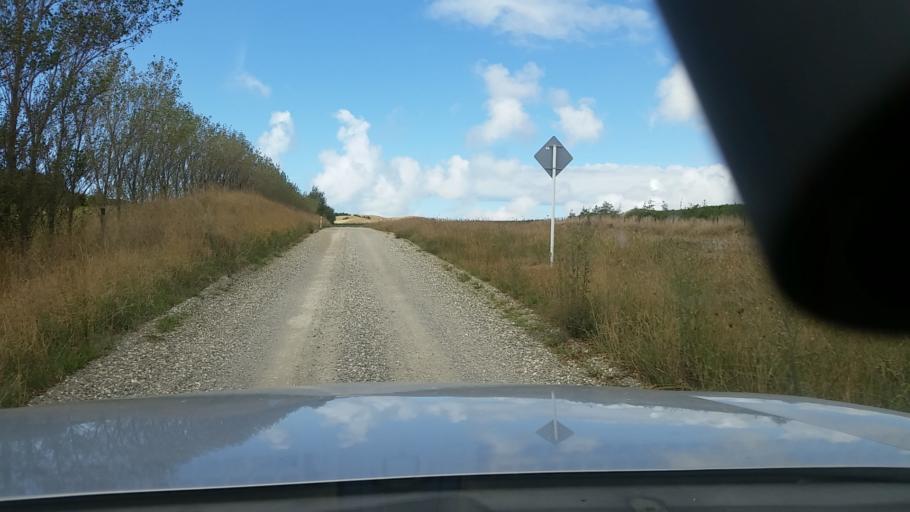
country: NZ
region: Marlborough
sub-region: Marlborough District
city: Blenheim
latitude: -41.6870
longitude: 174.1323
